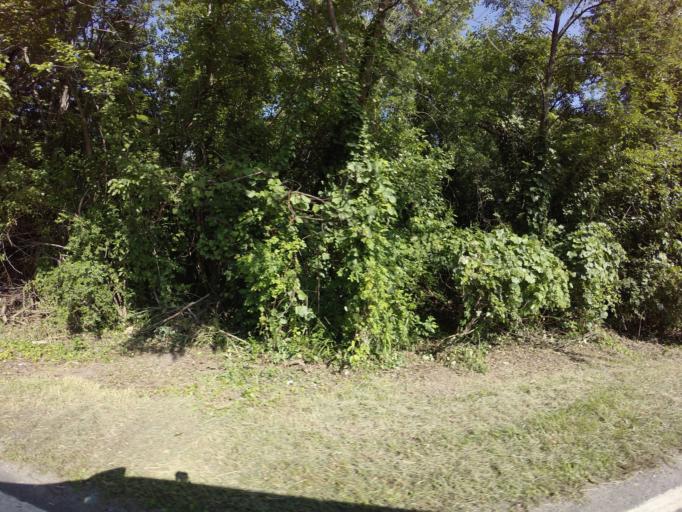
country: US
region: Maryland
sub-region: Baltimore County
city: Edgemere
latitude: 39.2051
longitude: -76.4438
